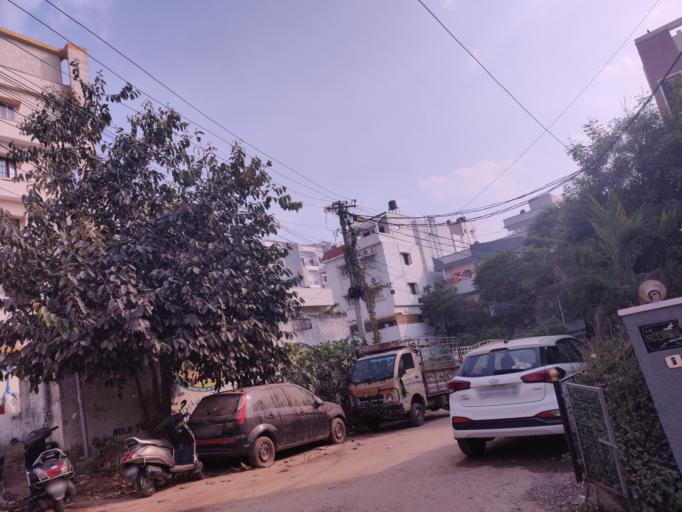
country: IN
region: Telangana
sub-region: Hyderabad
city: Hyderabad
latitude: 17.4045
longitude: 78.3922
